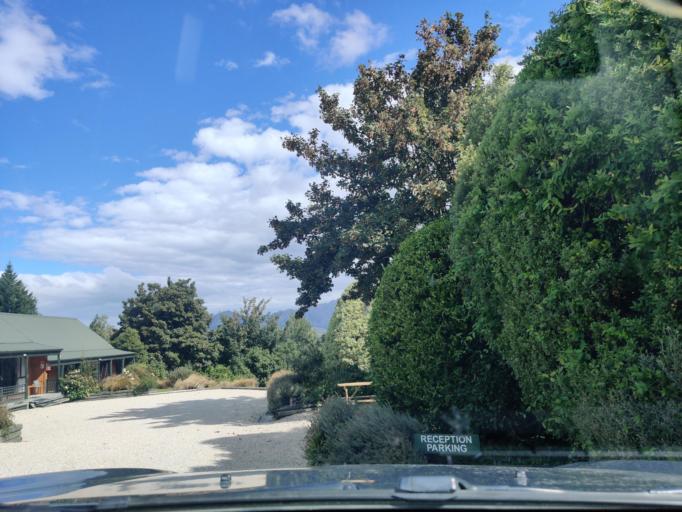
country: NZ
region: Canterbury
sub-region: Hurunui District
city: Amberley
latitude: -42.5258
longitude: 172.8295
